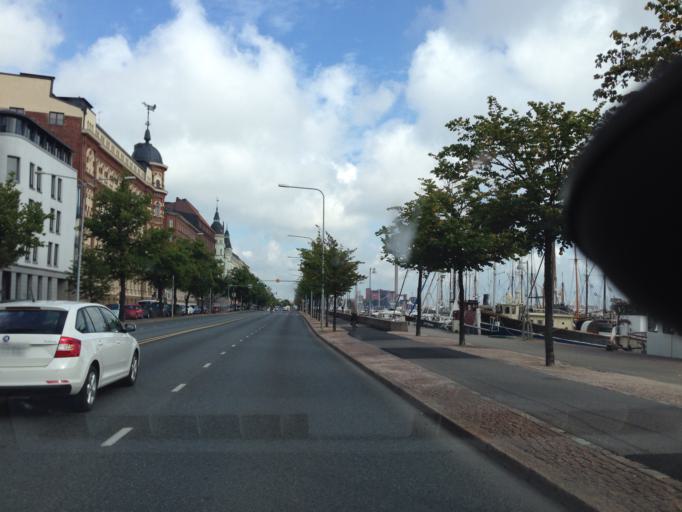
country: FI
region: Uusimaa
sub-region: Helsinki
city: Helsinki
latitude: 60.1698
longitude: 24.9598
